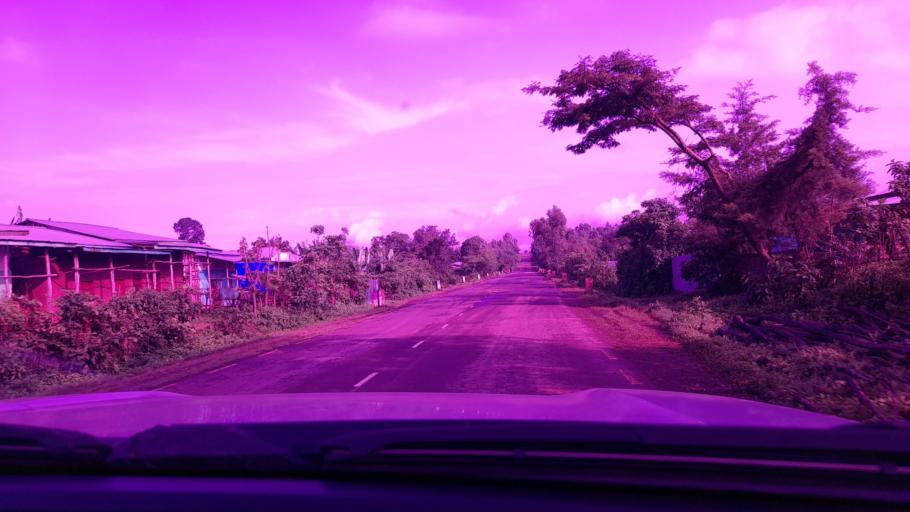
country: ET
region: Oromiya
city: Bedele
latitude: 8.1842
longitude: 36.4518
